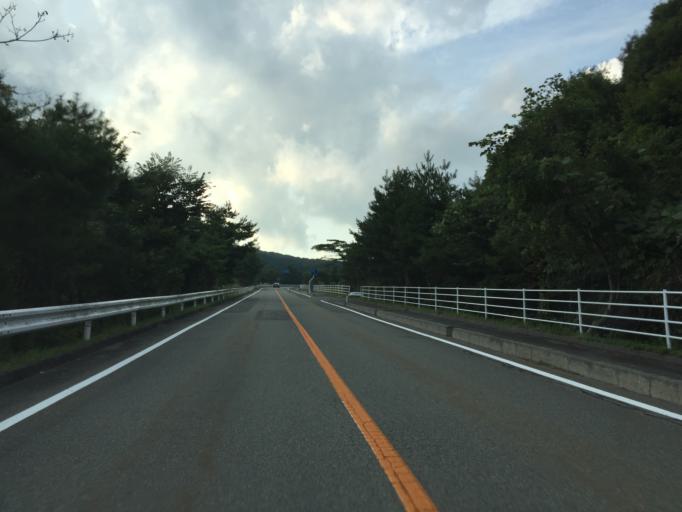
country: JP
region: Fukushima
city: Funehikimachi-funehiki
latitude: 37.5730
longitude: 140.7326
